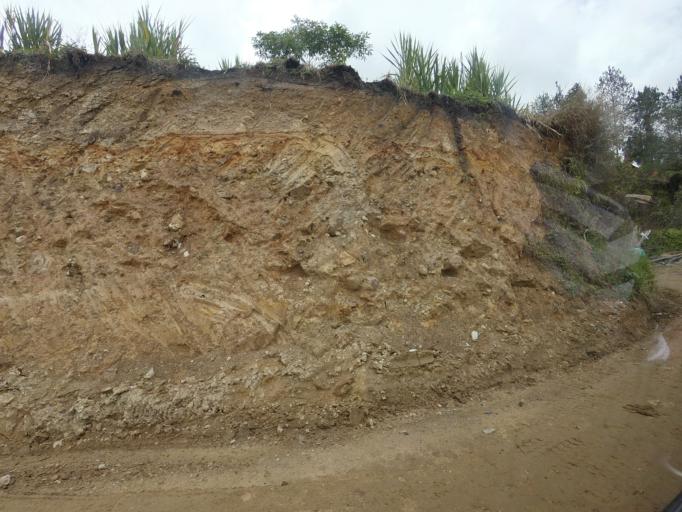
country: CO
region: Huila
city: San Agustin
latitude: 1.9572
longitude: -76.2971
